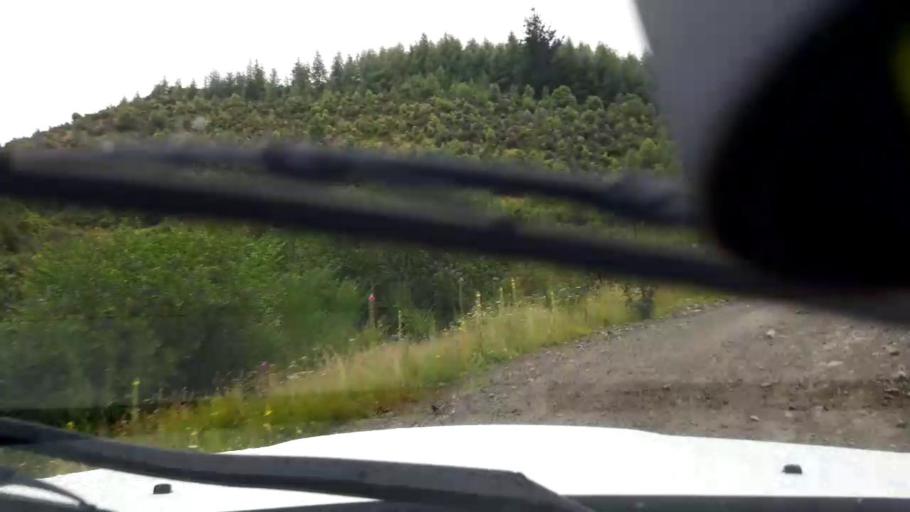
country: NZ
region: Canterbury
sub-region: Timaru District
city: Pleasant Point
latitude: -44.0437
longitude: 171.0177
